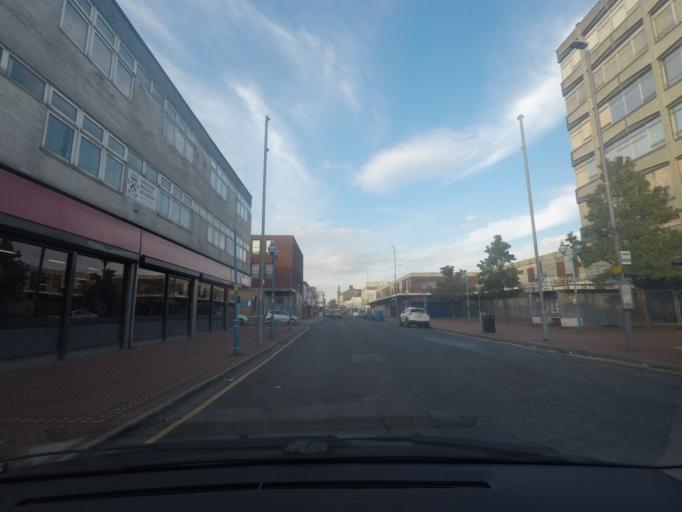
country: GB
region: England
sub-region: North East Lincolnshire
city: Grimsby
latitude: 53.5730
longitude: -0.0732
